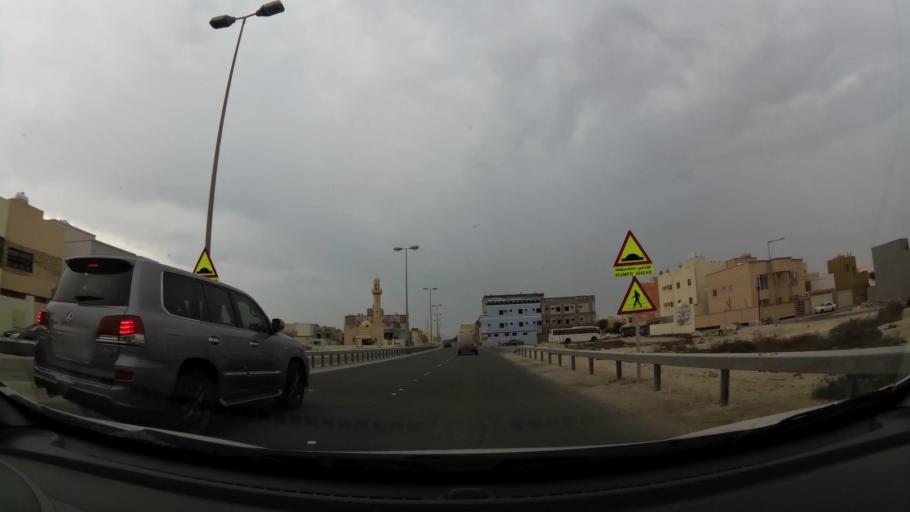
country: BH
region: Central Governorate
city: Madinat Hamad
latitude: 26.0964
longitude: 50.4978
